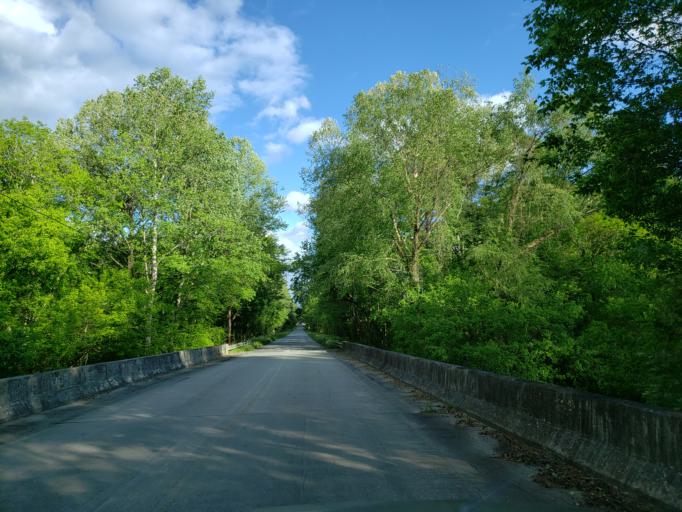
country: US
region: Georgia
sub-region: Haralson County
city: Tallapoosa
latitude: 33.7776
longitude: -85.3099
